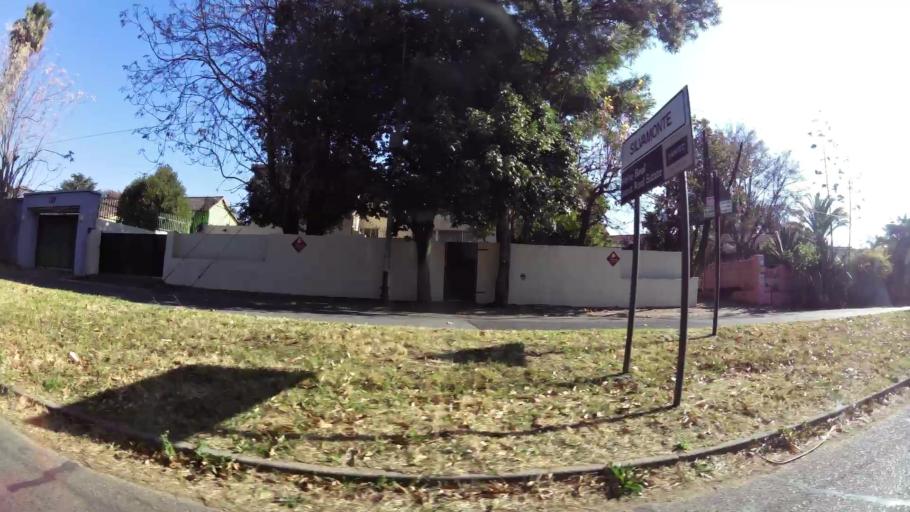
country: ZA
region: Gauteng
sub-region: City of Johannesburg Metropolitan Municipality
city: Modderfontein
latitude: -26.1396
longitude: 28.1149
